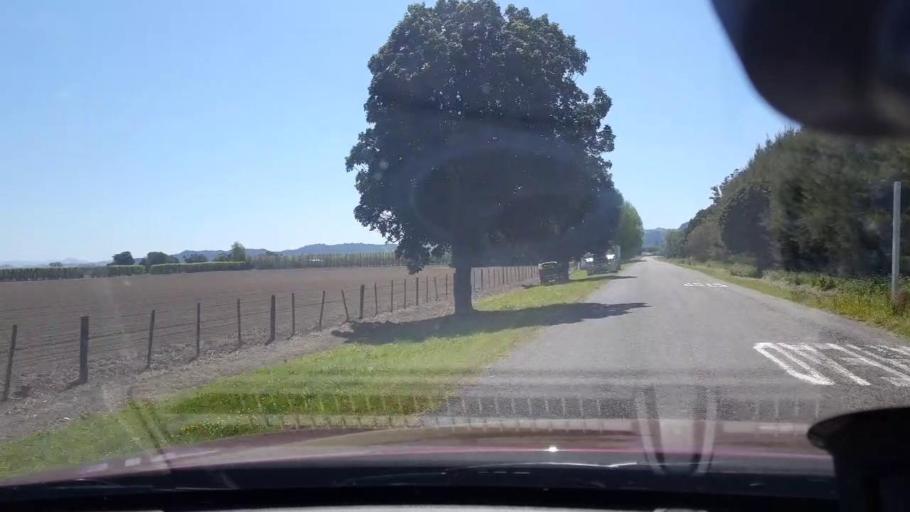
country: NZ
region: Gisborne
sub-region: Gisborne District
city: Gisborne
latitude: -38.6402
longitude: 177.9377
